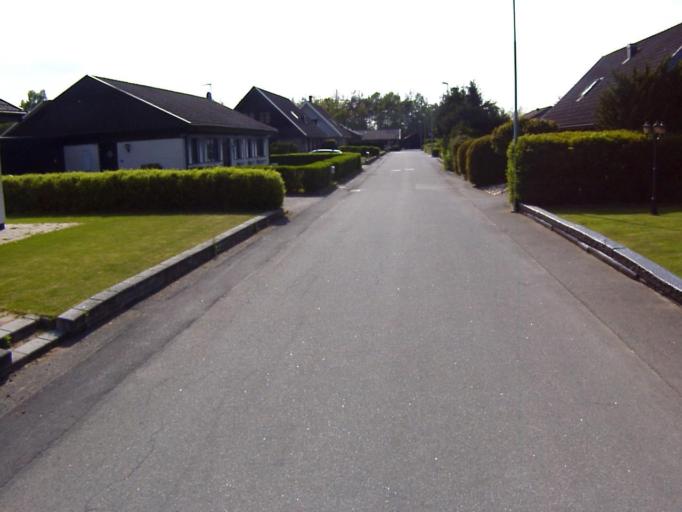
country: SE
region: Skane
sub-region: Kristianstads Kommun
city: Kristianstad
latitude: 56.0619
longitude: 14.0876
